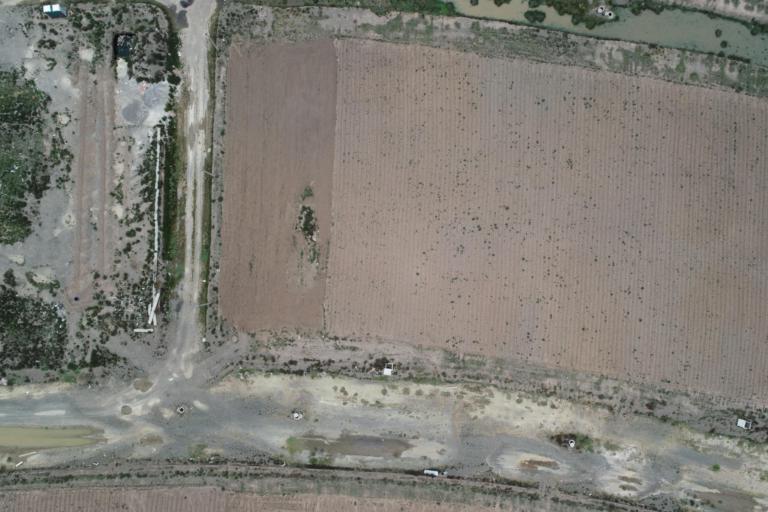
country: BO
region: La Paz
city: La Paz
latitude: -16.5178
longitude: -68.3000
